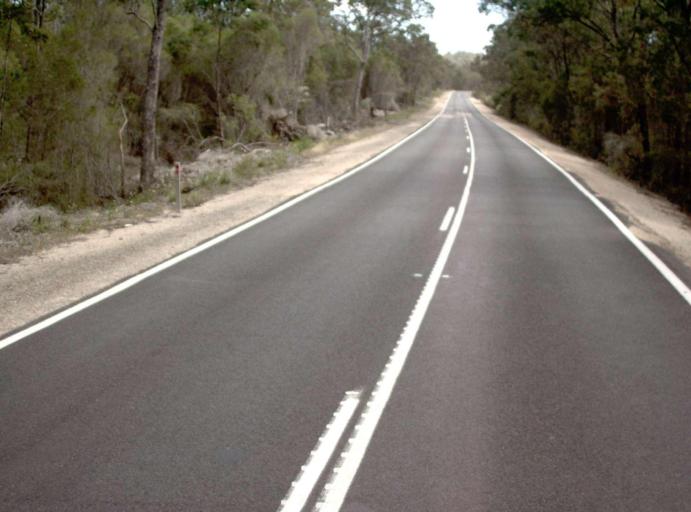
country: AU
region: New South Wales
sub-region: Bega Valley
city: Eden
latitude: -37.4508
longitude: 149.6202
